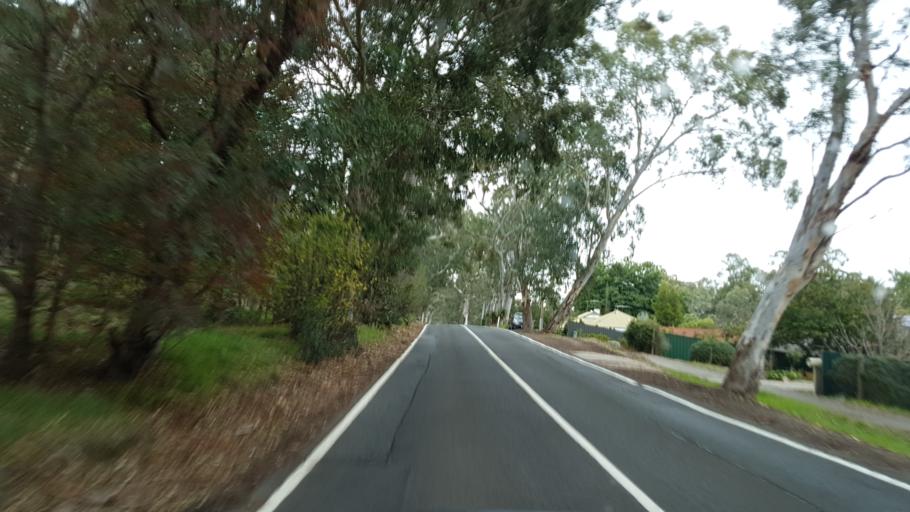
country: AU
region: South Australia
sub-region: Mitcham
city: Belair
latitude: -35.0039
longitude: 138.6332
